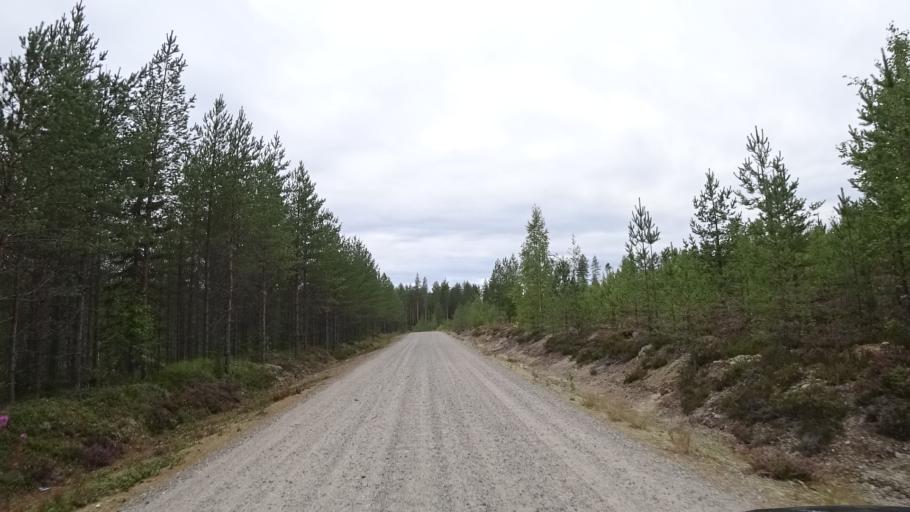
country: FI
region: North Karelia
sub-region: Joensuu
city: Ilomantsi
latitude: 63.1547
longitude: 30.6369
